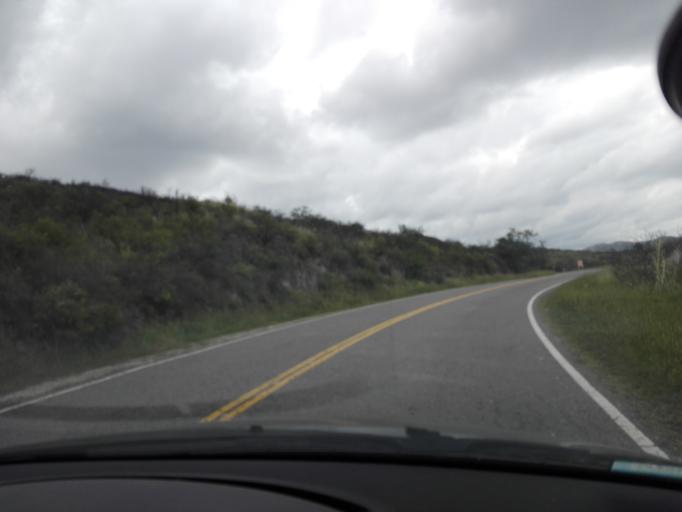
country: AR
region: Cordoba
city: Alta Gracia
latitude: -31.5915
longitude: -64.5058
